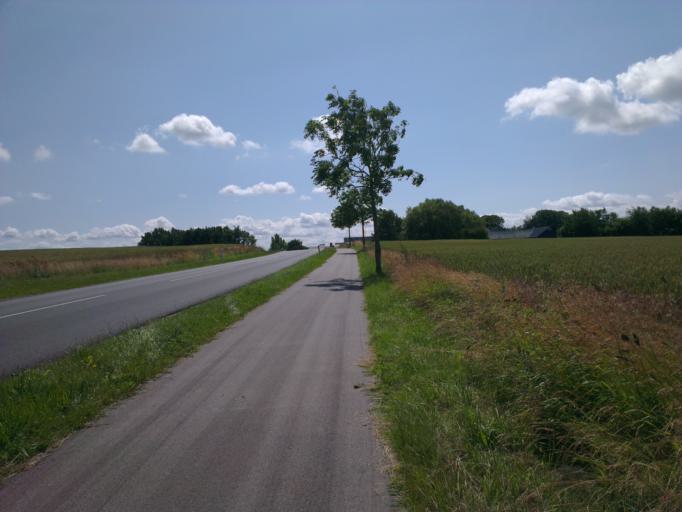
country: DK
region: Capital Region
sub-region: Frederikssund Kommune
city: Skibby
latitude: 55.7709
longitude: 11.9067
